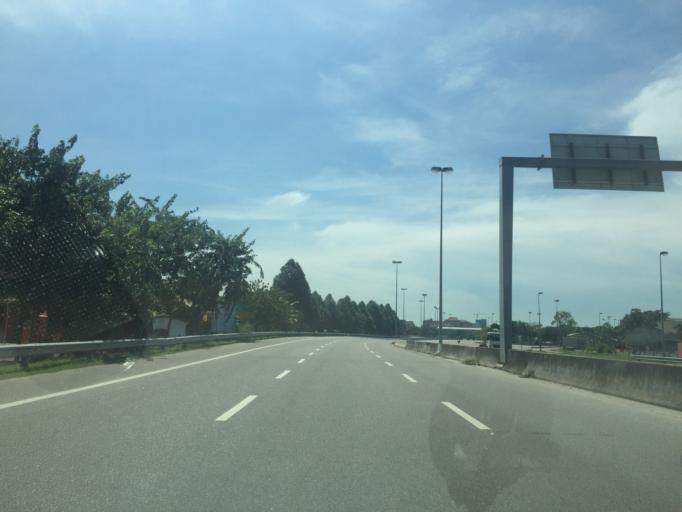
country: MY
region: Penang
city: Permatang Kuching
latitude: 5.4361
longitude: 100.3782
